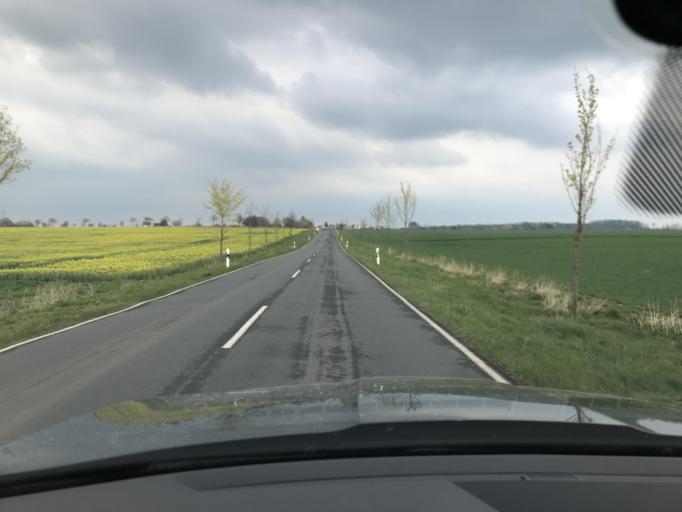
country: DE
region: Saxony-Anhalt
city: Ballenstedt
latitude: 51.7521
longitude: 11.2386
